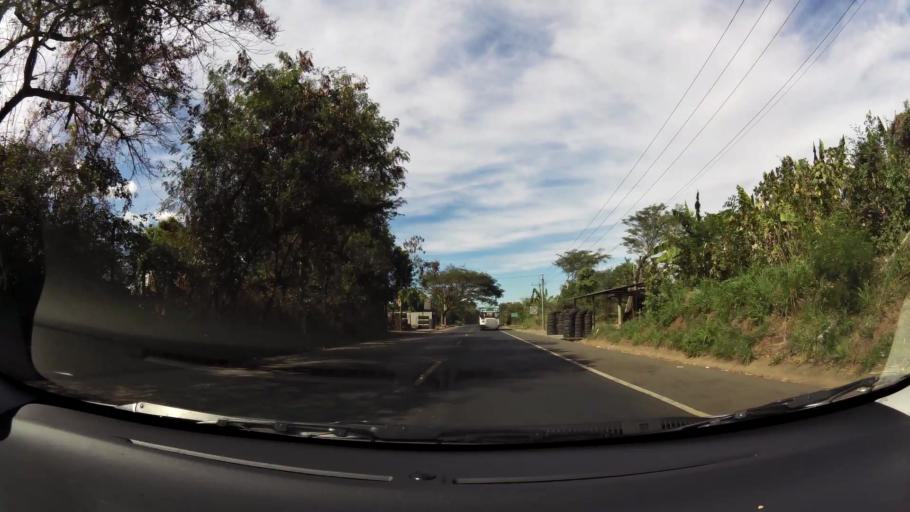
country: SV
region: San Salvador
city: Guazapa
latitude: 13.9129
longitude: -89.1821
